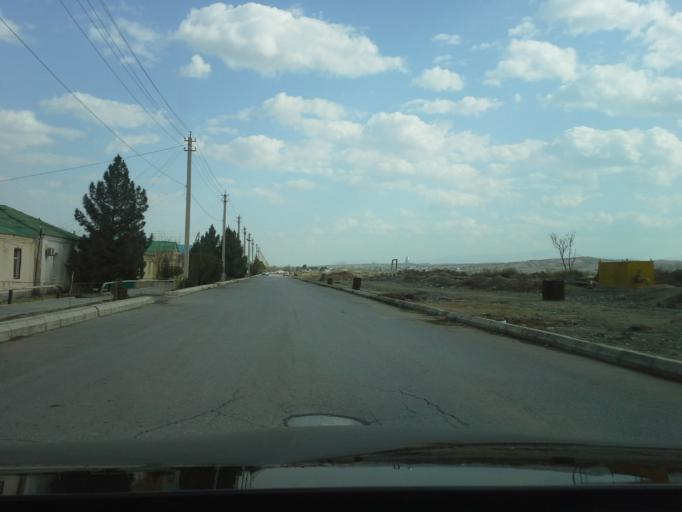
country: TM
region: Ahal
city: Ashgabat
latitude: 37.9850
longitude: 58.2837
